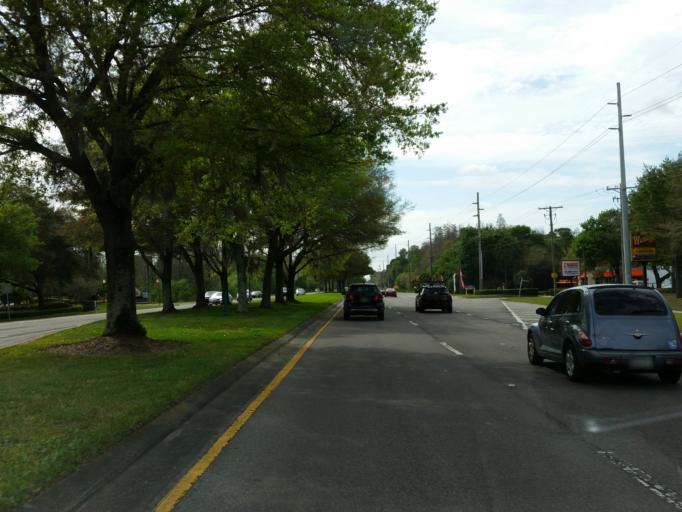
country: US
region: Florida
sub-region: Hillsborough County
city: Temple Terrace
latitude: 28.0693
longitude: -82.3612
